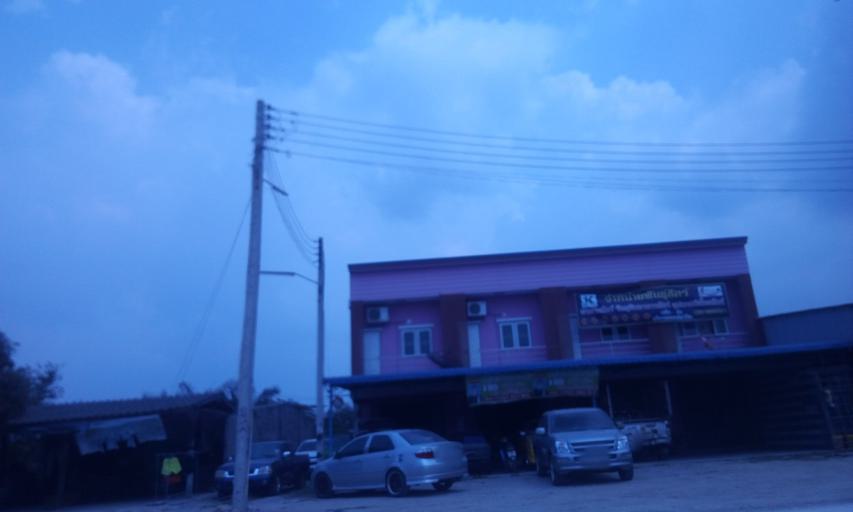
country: TH
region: Chon Buri
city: Ban Bueng
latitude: 13.3254
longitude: 101.1865
